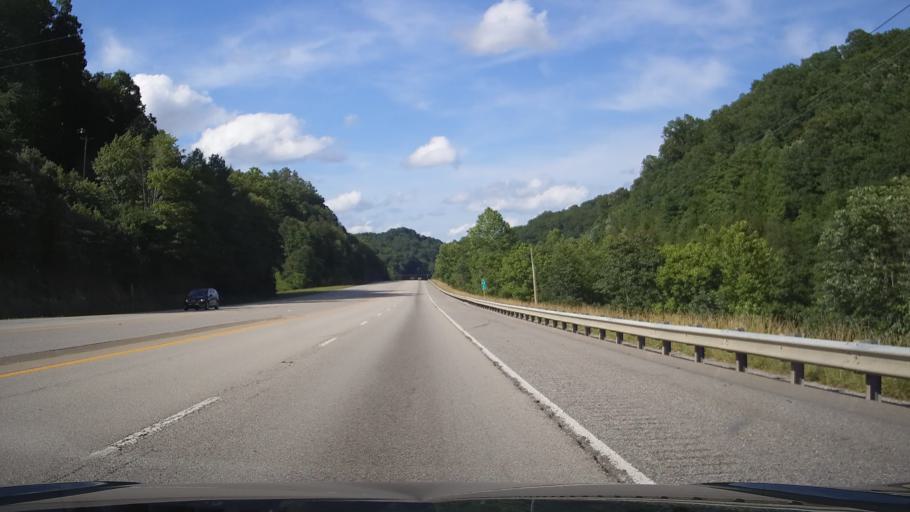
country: US
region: Kentucky
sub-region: Lawrence County
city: Louisa
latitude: 38.0408
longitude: -82.6483
